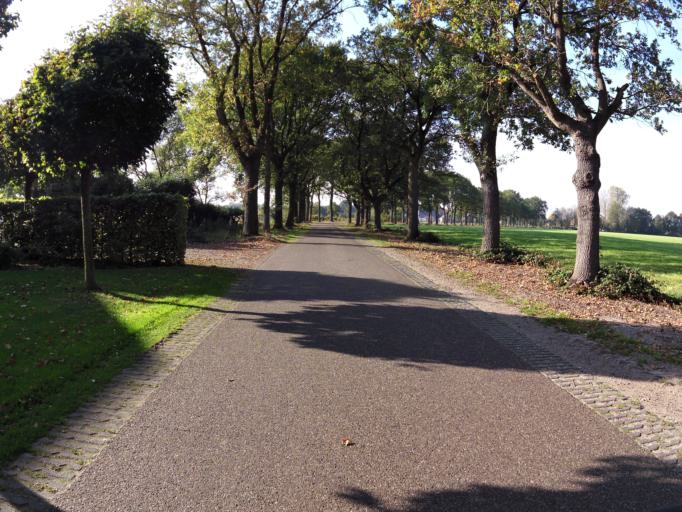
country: NL
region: North Brabant
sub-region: Gemeente Helmond
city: Helmond
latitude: 51.5263
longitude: 5.6902
